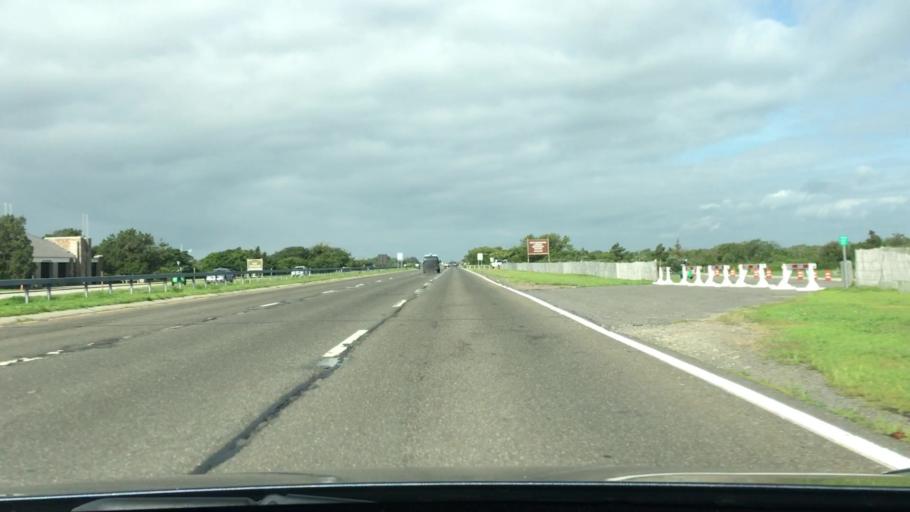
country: US
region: New York
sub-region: Nassau County
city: Point Lookout
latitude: 40.5961
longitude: -73.5135
